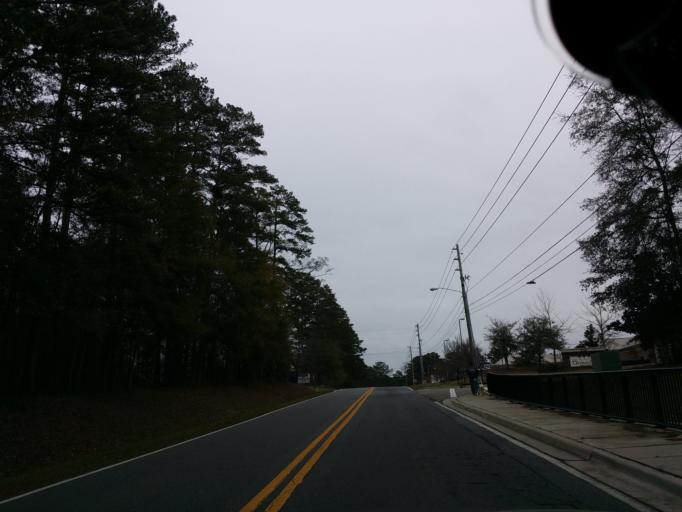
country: US
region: Florida
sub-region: Leon County
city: Tallahassee
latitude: 30.4798
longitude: -84.2242
